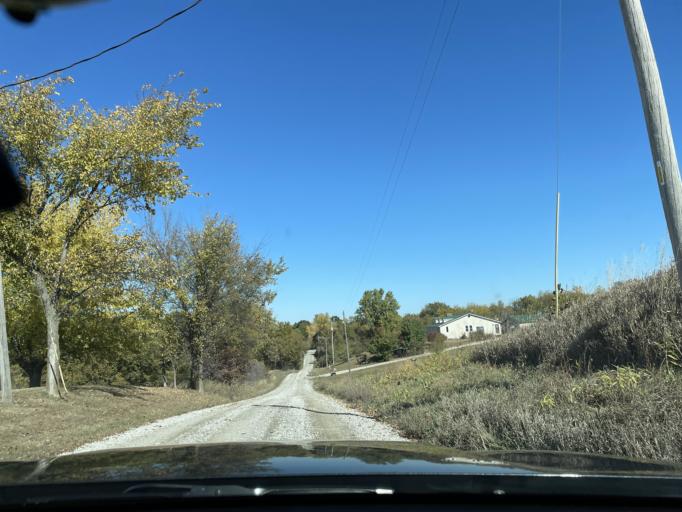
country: US
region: Missouri
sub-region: Andrew County
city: Savannah
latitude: 39.9331
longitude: -94.8804
